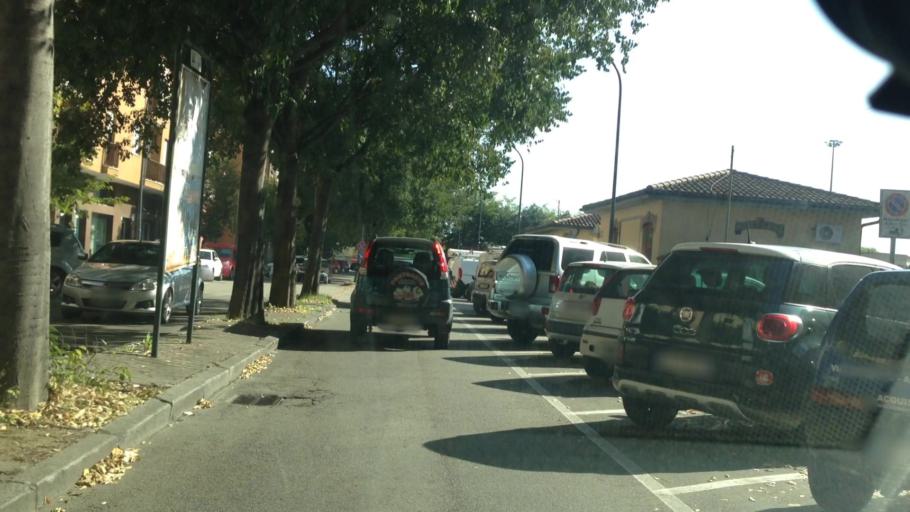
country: IT
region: Piedmont
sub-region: Provincia di Asti
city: Asti
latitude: 44.8977
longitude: 8.2147
